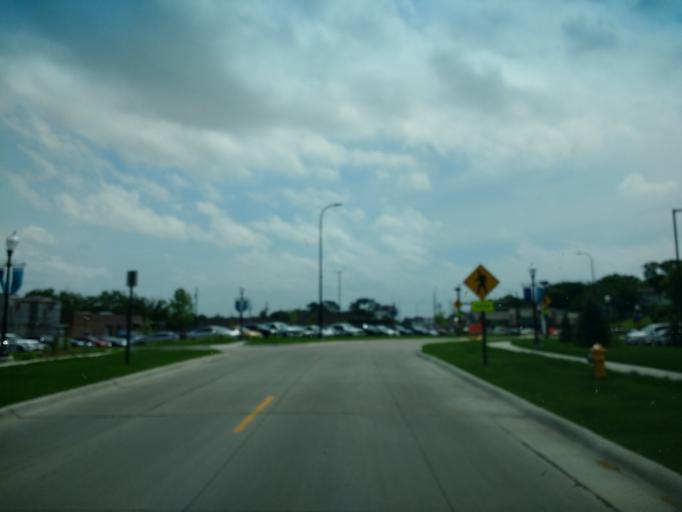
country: US
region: Iowa
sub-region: Woodbury County
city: Sioux City
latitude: 42.5192
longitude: -96.4048
